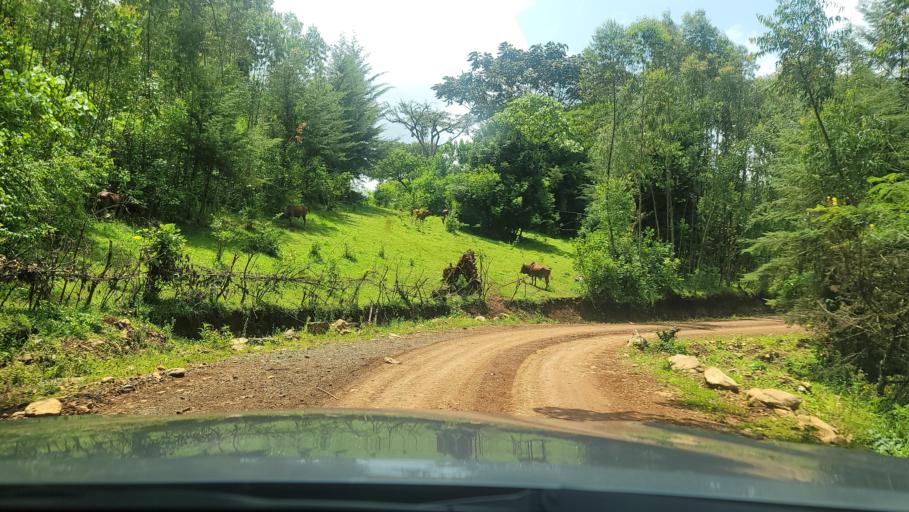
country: ET
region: Oromiya
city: Agaro
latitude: 7.7356
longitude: 36.2606
